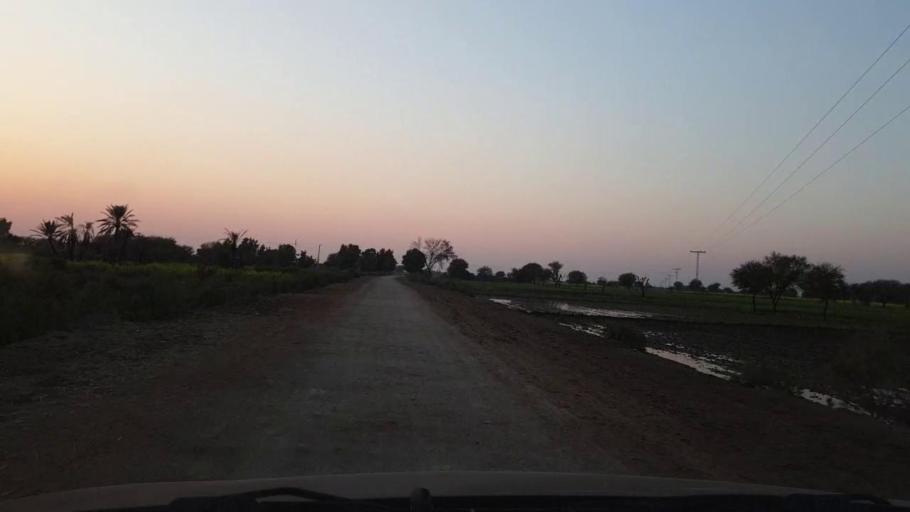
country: PK
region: Sindh
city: Jhol
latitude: 25.9371
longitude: 68.9601
